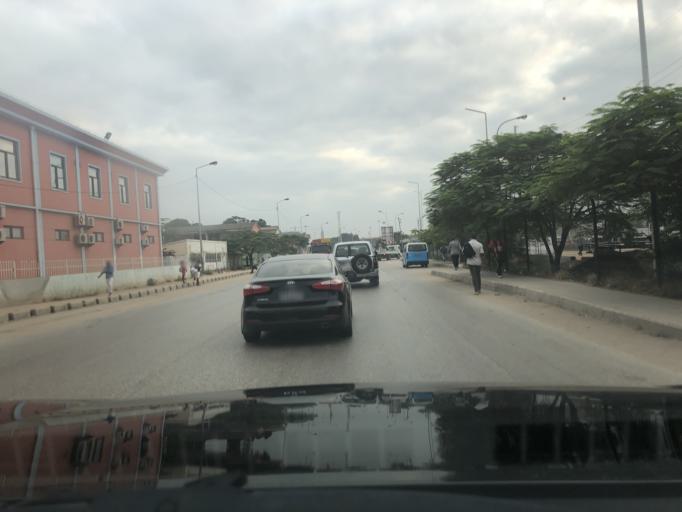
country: AO
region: Luanda
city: Luanda
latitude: -8.8383
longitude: 13.2540
